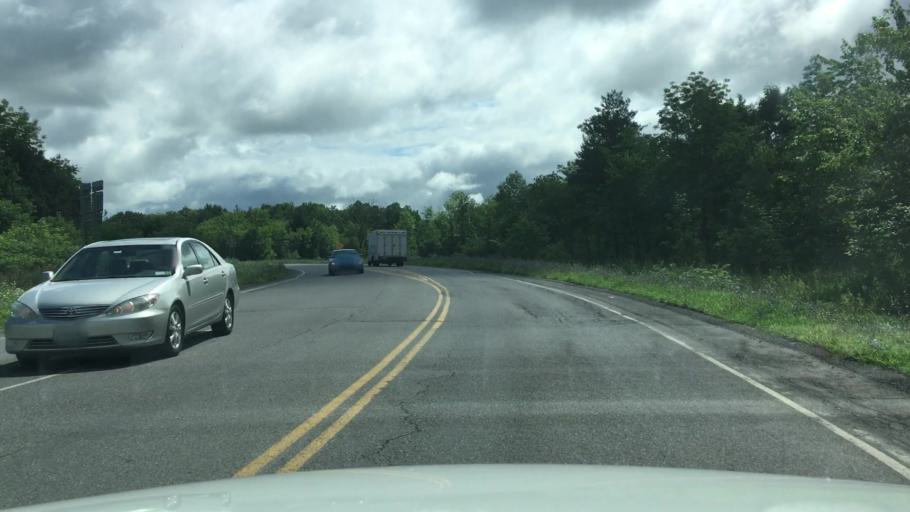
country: US
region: New York
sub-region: Schenectady County
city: Scotia
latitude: 42.8375
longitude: -73.9520
